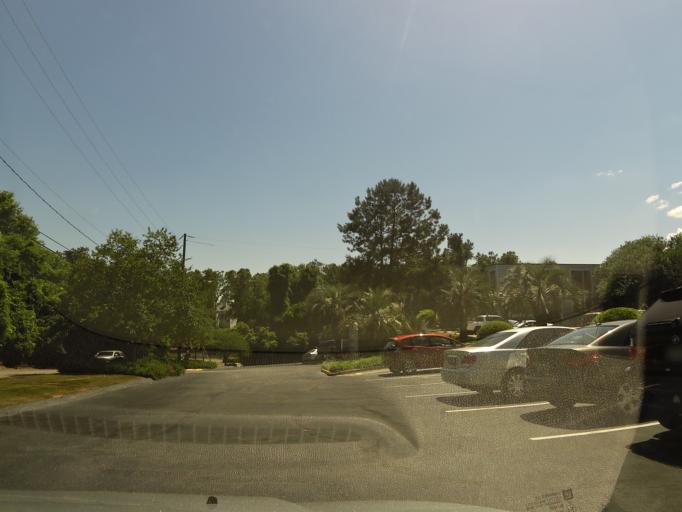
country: US
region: South Carolina
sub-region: Aiken County
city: Aiken
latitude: 33.5569
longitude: -81.7248
